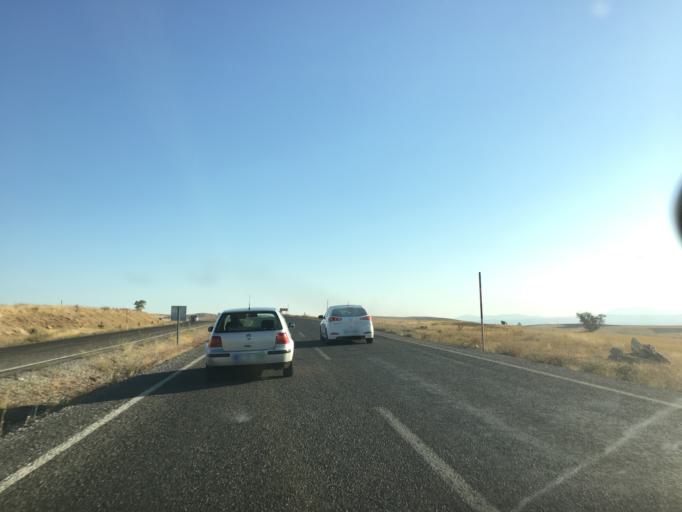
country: TR
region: Nevsehir
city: Hacibektas
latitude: 38.9225
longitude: 34.5452
